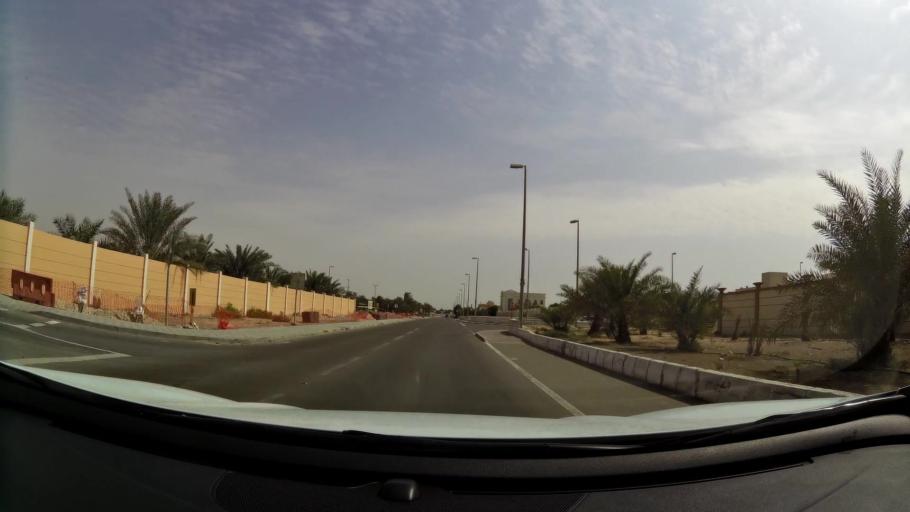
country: AE
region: Abu Dhabi
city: Abu Dhabi
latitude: 24.5460
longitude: 54.6712
